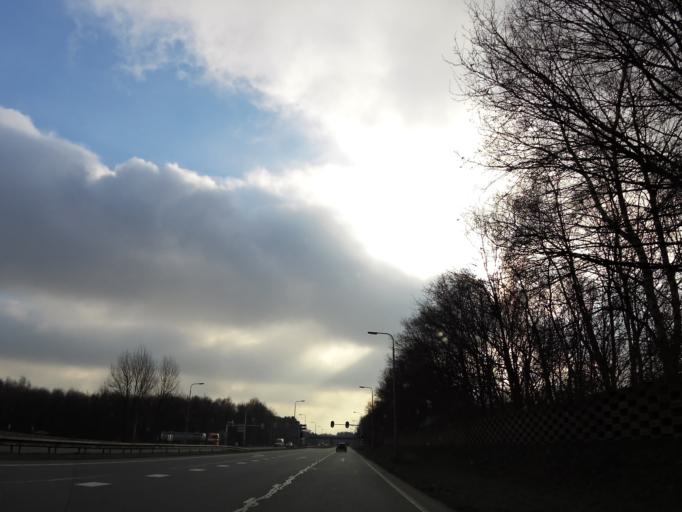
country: NL
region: Limburg
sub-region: Gemeente Gennep
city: Gennep
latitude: 51.6703
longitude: 5.9874
